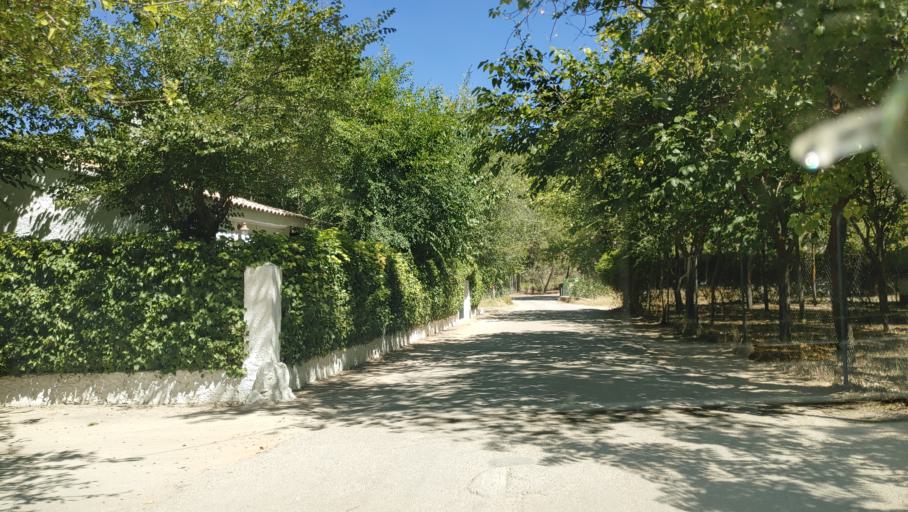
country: ES
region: Castille-La Mancha
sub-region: Provincia de Ciudad Real
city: Ruidera
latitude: 38.9271
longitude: -2.8293
